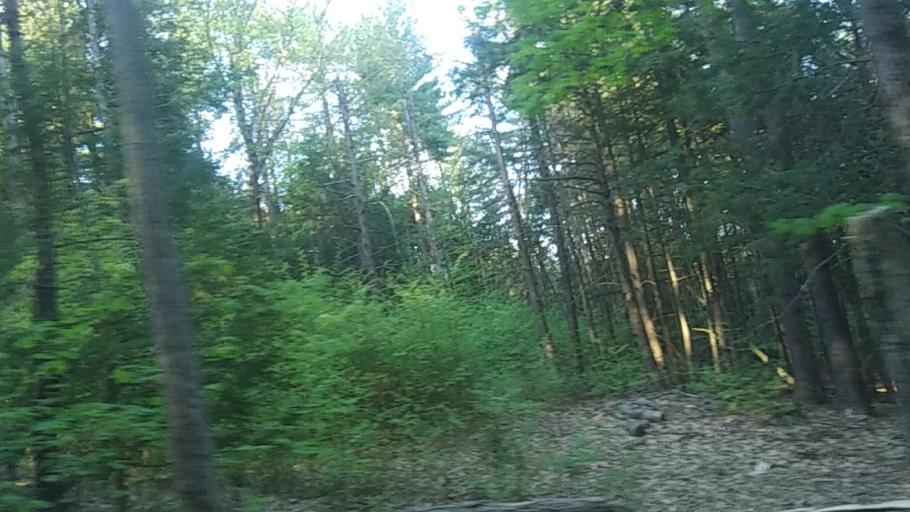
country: US
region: Massachusetts
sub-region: Franklin County
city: Buckland
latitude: 42.5708
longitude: -72.7697
